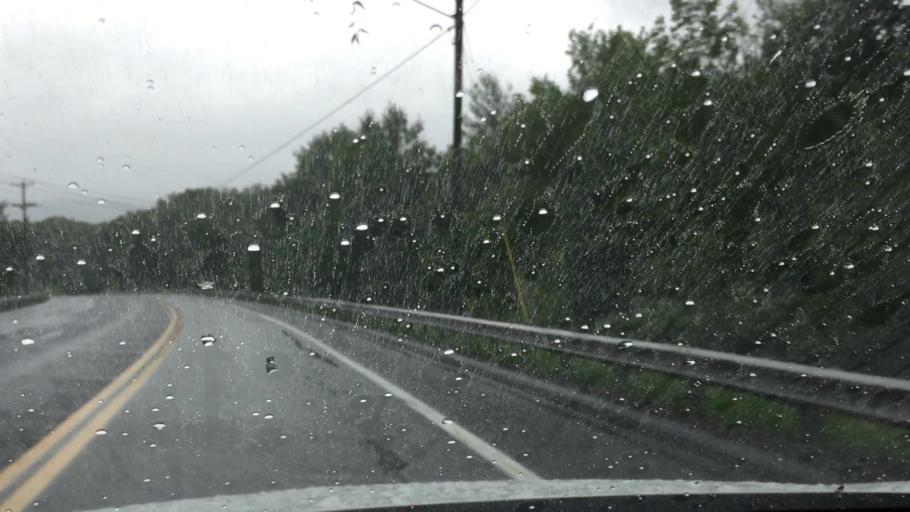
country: US
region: Massachusetts
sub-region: Berkshire County
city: Lanesborough
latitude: 42.4962
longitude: -73.2265
